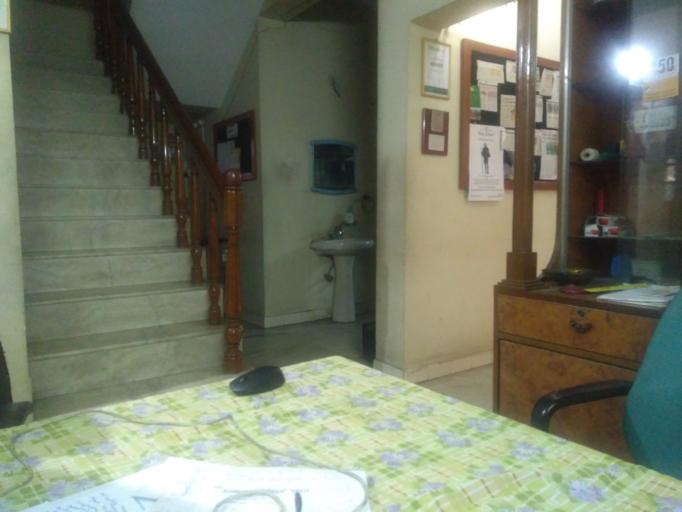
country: IN
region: Karnataka
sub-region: Bangalore Urban
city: Bangalore
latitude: 12.9200
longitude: 77.5626
